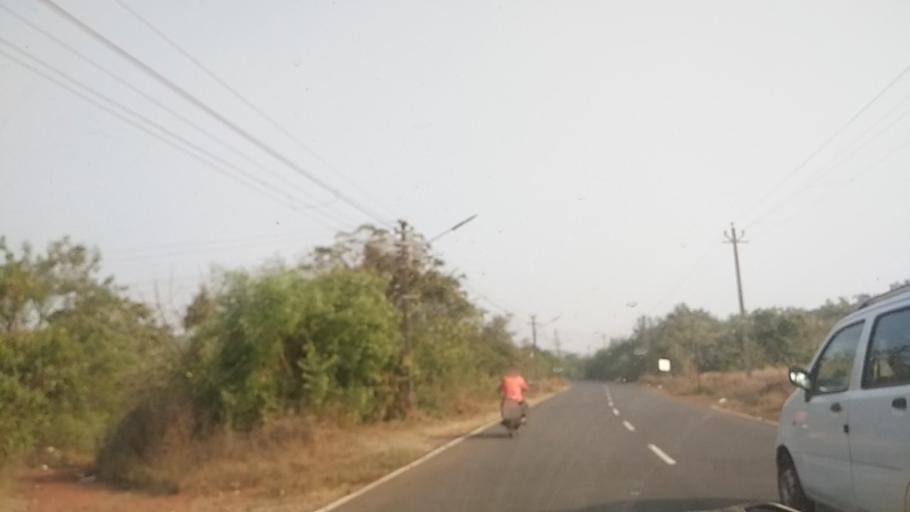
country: IN
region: Goa
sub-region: North Goa
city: Morjim
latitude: 15.6562
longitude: 73.7500
